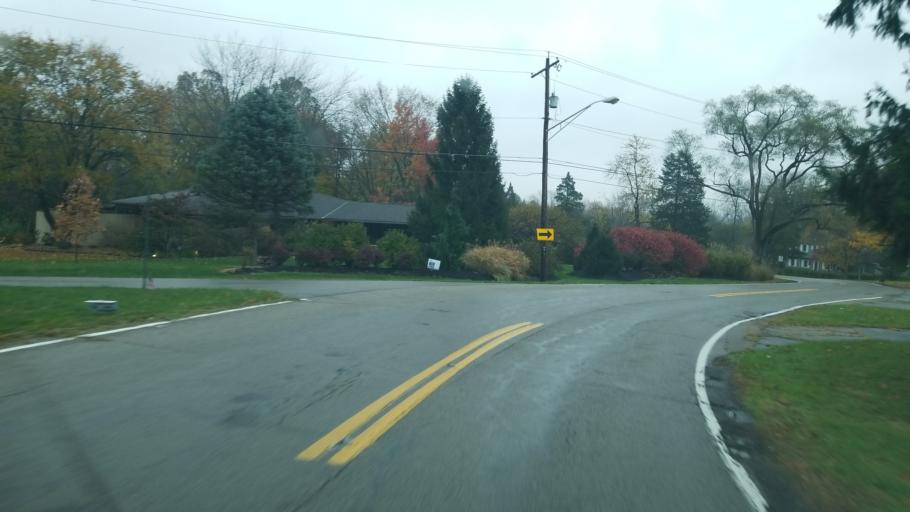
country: US
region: Ohio
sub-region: Franklin County
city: Upper Arlington
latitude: 40.0397
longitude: -83.0399
